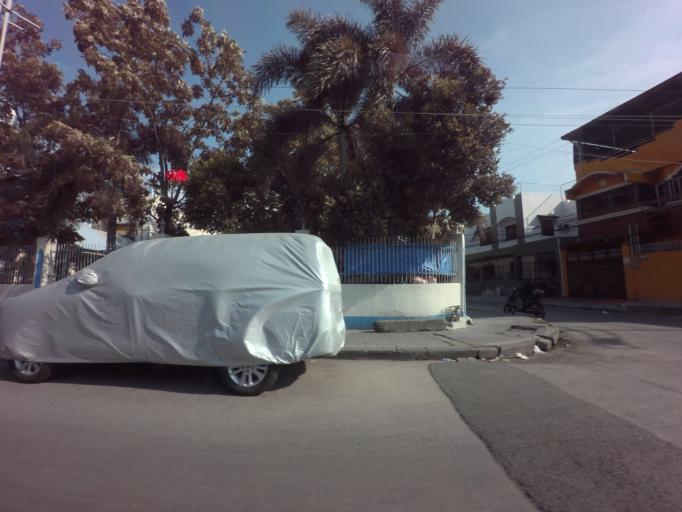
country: PH
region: Calabarzon
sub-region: Province of Rizal
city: Taguig
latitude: 14.4974
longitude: 121.0529
